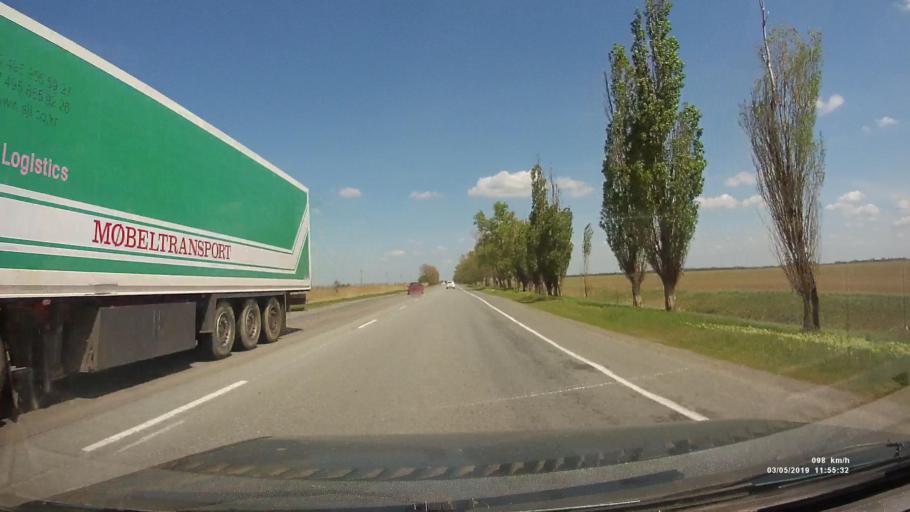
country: RU
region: Rostov
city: Bagayevskaya
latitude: 47.1825
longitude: 40.2922
